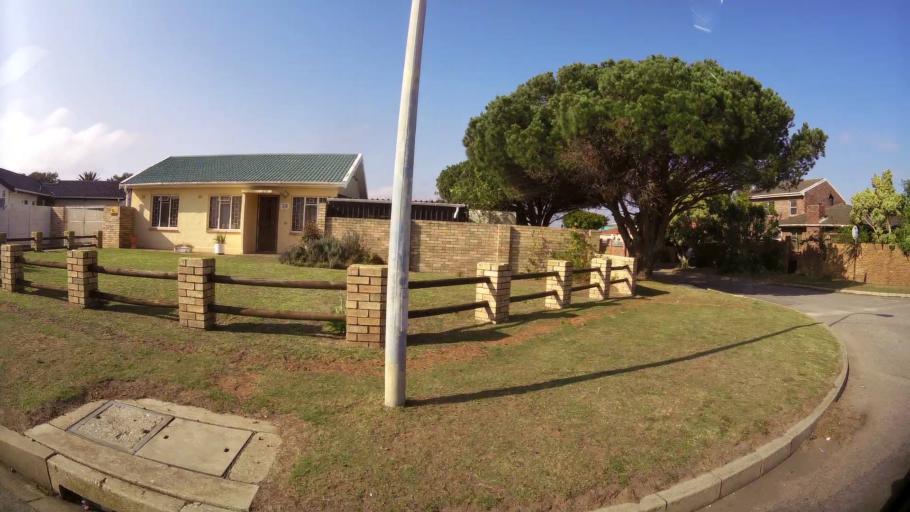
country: ZA
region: Eastern Cape
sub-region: Nelson Mandela Bay Metropolitan Municipality
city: Port Elizabeth
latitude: -33.9218
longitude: 25.5258
